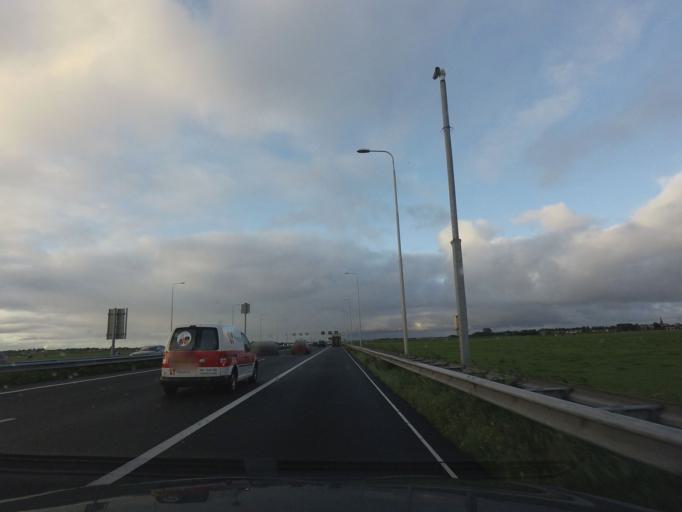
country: NL
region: North Holland
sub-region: Gemeente Heiloo
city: Heiloo
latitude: 52.5799
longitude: 4.7182
